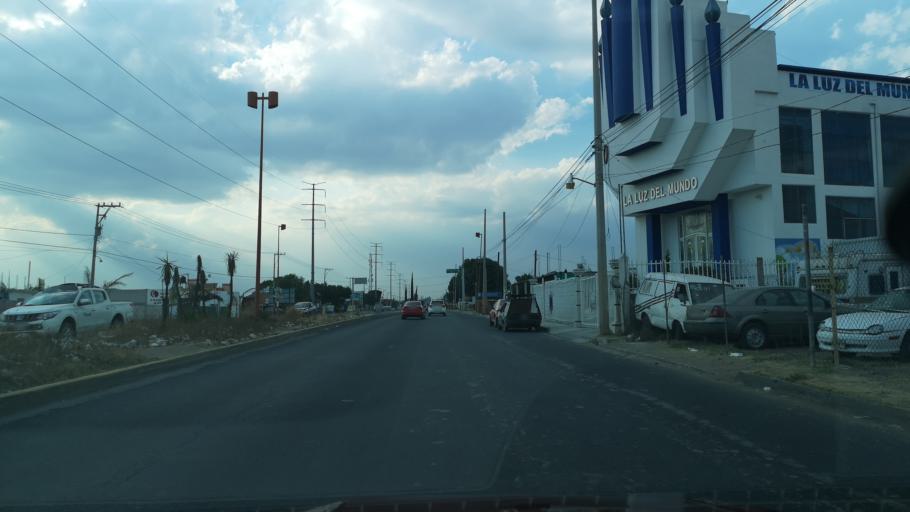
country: MX
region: Puebla
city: Cuanala
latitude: 19.0848
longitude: -98.3309
